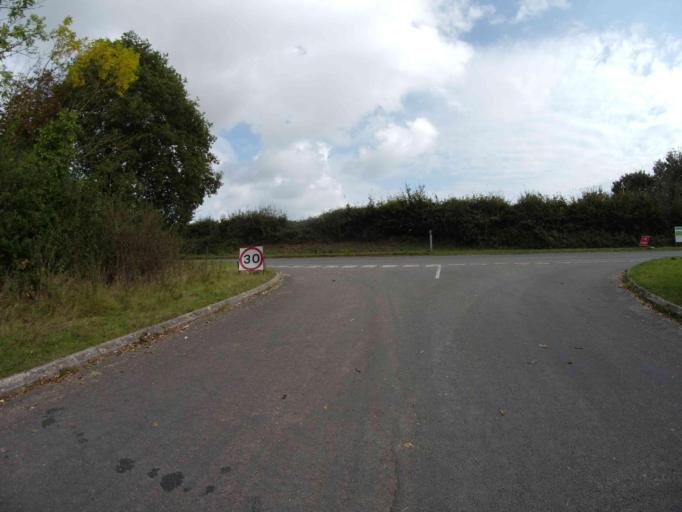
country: GB
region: England
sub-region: Devon
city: Budleigh Salterton
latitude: 50.6404
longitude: -3.3176
